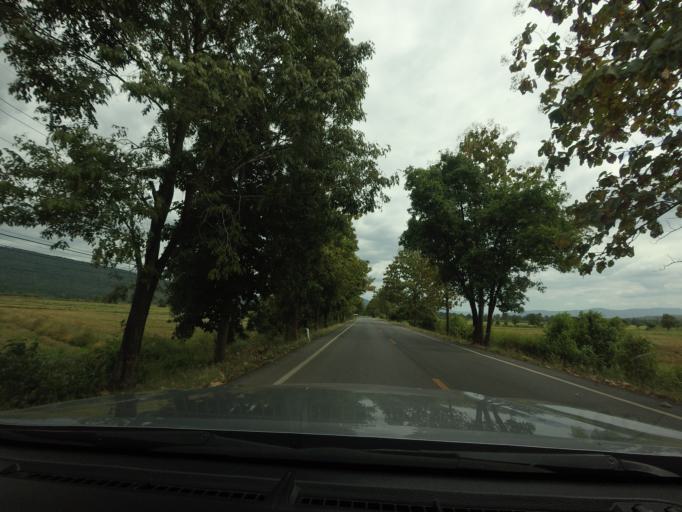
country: TH
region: Phitsanulok
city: Noen Maprang
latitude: 16.6925
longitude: 100.5489
